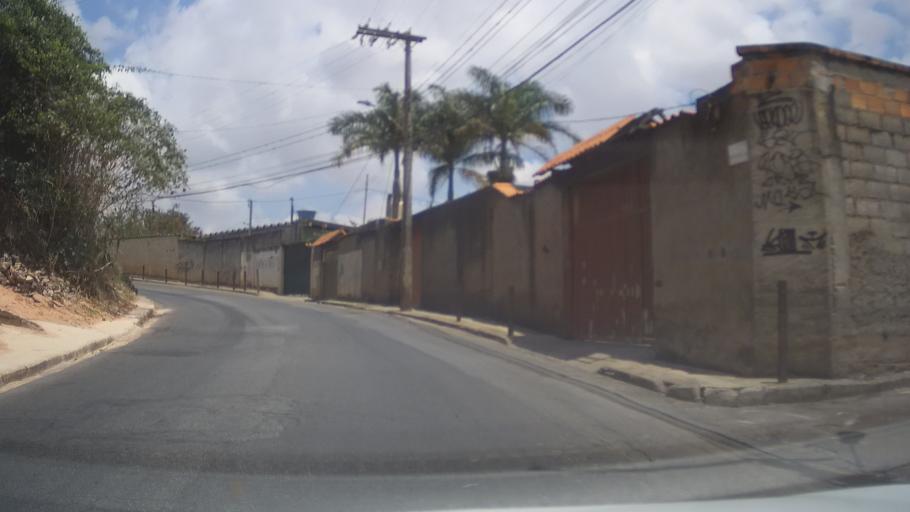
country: BR
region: Minas Gerais
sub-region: Belo Horizonte
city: Belo Horizonte
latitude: -19.9036
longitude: -43.8832
